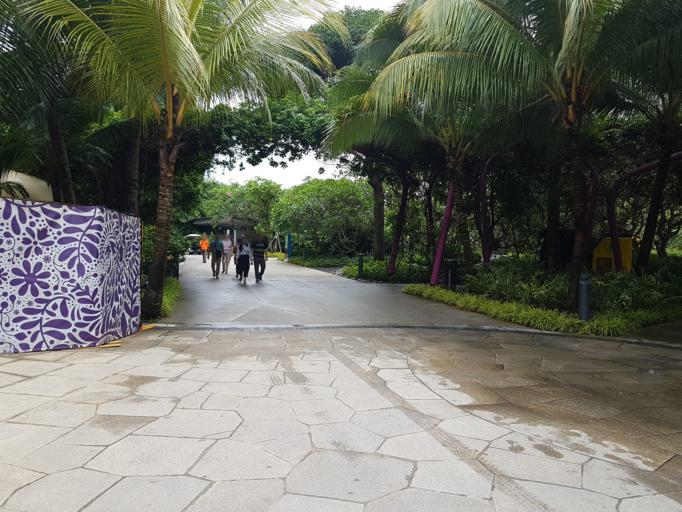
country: SG
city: Singapore
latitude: 1.2824
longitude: 103.8630
